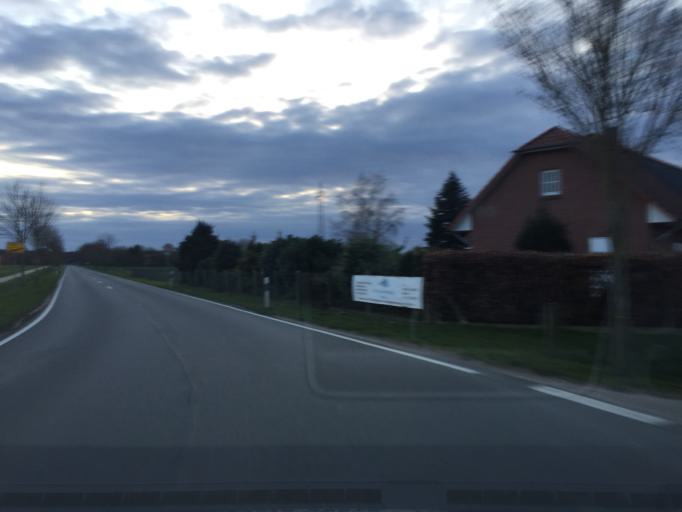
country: DE
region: Lower Saxony
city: Steimbke
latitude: 52.5769
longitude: 9.4173
